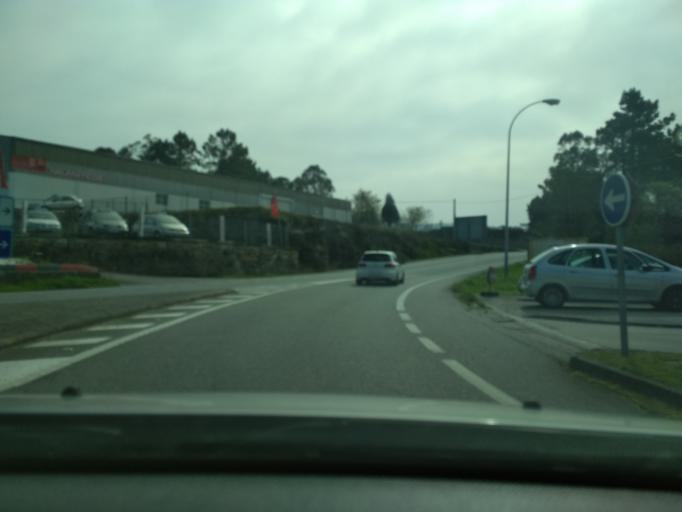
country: ES
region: Galicia
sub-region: Provincia de Pontevedra
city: Catoira
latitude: 42.6717
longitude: -8.7097
